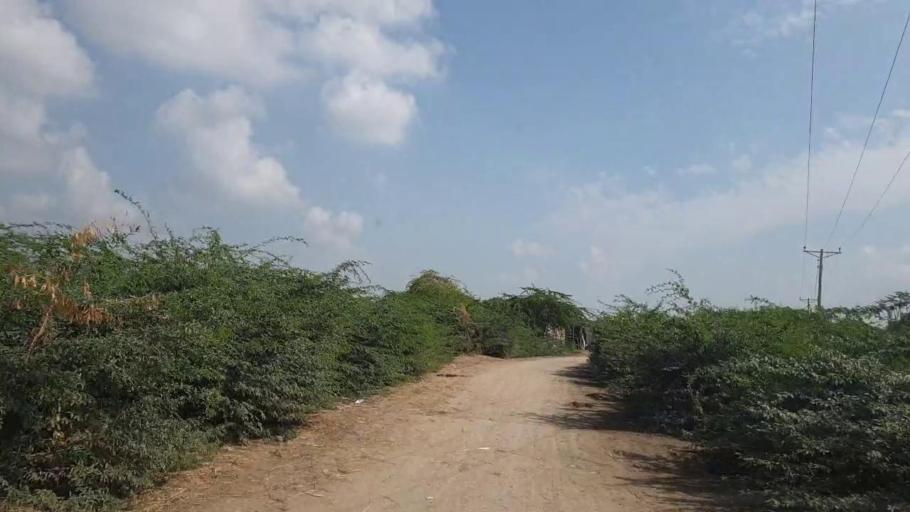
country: PK
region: Sindh
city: Badin
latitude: 24.4790
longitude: 68.6129
